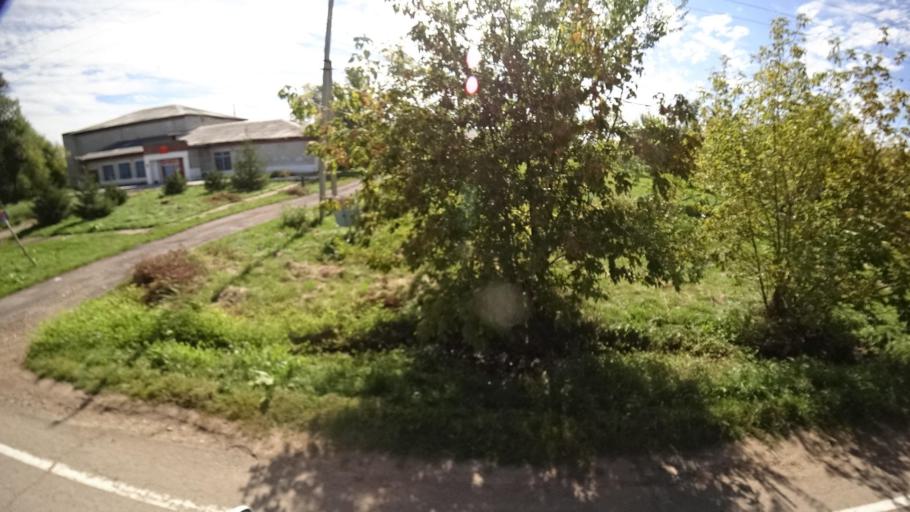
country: RU
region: Primorskiy
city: Yakovlevka
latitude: 44.4325
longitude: 133.5651
